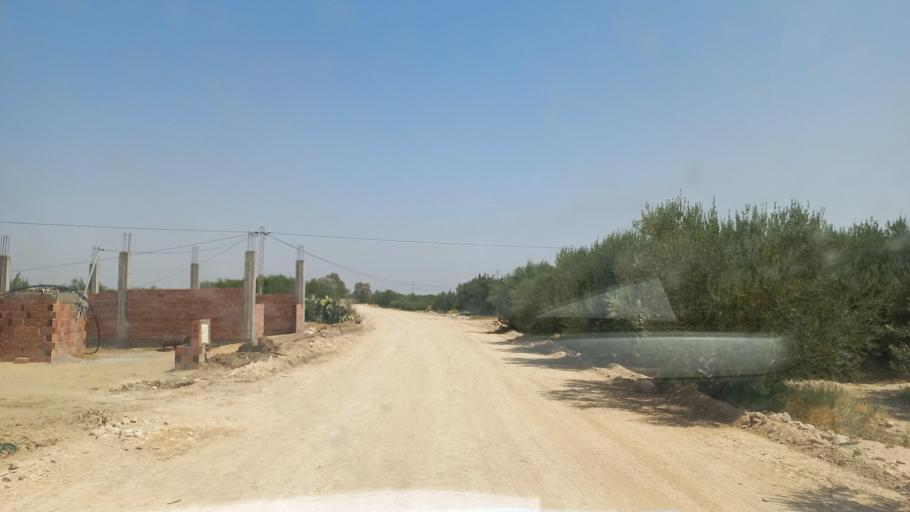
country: TN
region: Al Qasrayn
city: Kasserine
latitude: 35.2470
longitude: 9.0256
